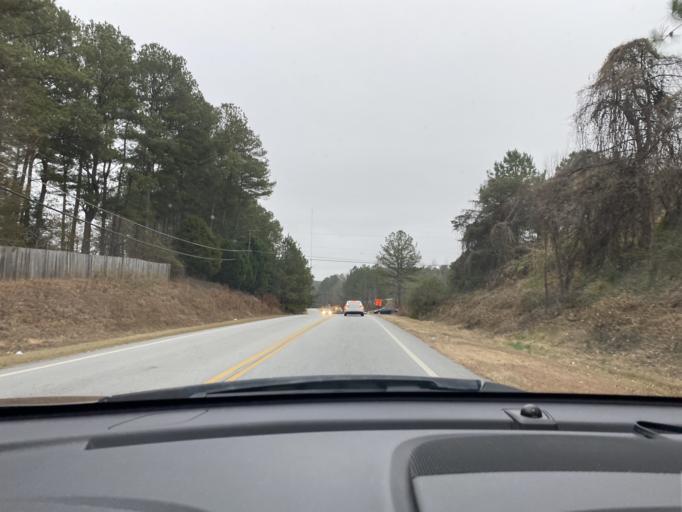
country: US
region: Georgia
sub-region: Gwinnett County
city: Grayson
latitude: 33.9056
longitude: -83.9239
